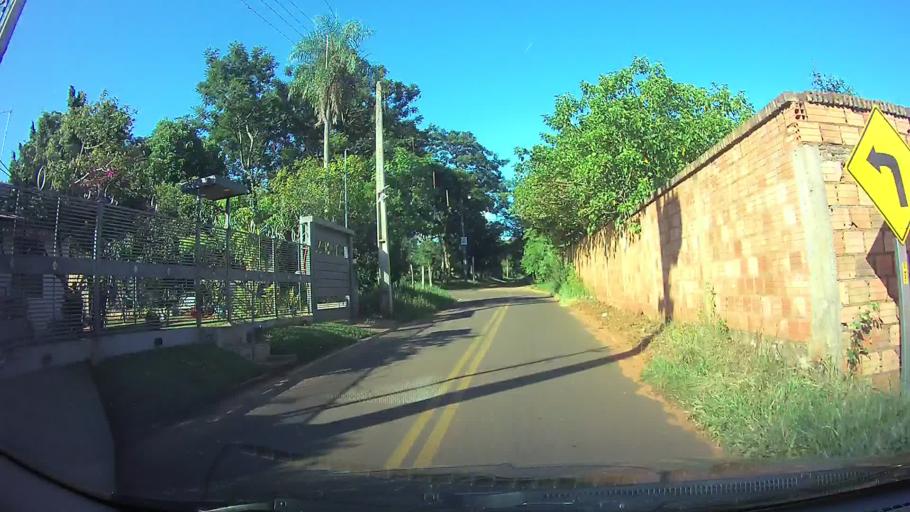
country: PY
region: Central
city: Aregua
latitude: -25.3531
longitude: -57.3943
